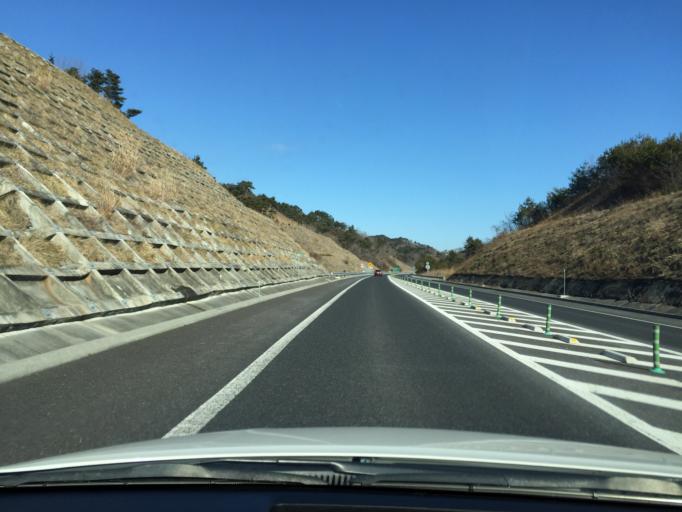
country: JP
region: Fukushima
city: Namie
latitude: 37.6818
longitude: 140.9173
